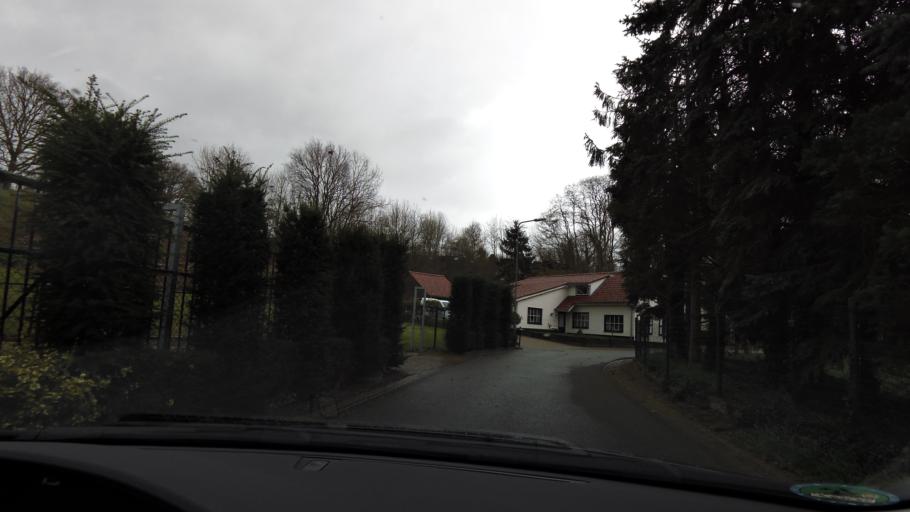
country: NL
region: Limburg
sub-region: Gemeente Beek
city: Beek
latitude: 50.9237
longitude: 5.8024
